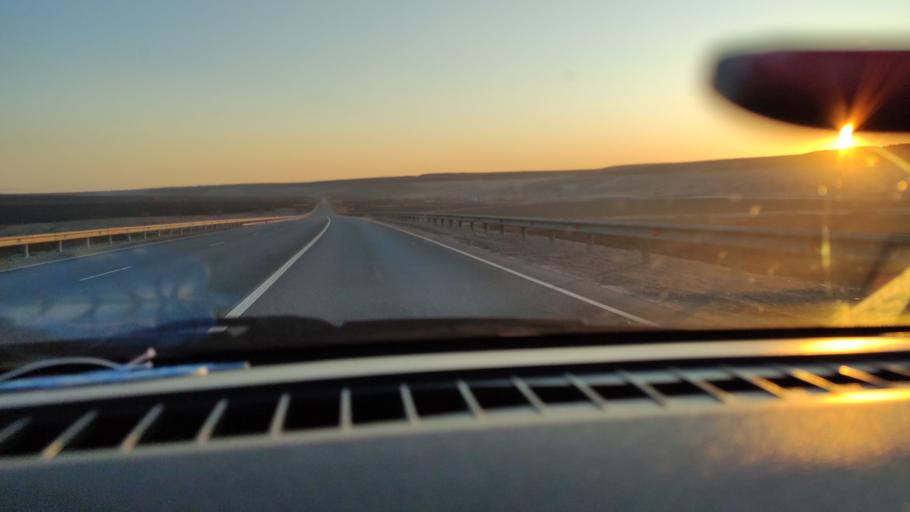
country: RU
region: Saratov
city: Yelshanka
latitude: 51.8393
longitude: 46.4761
